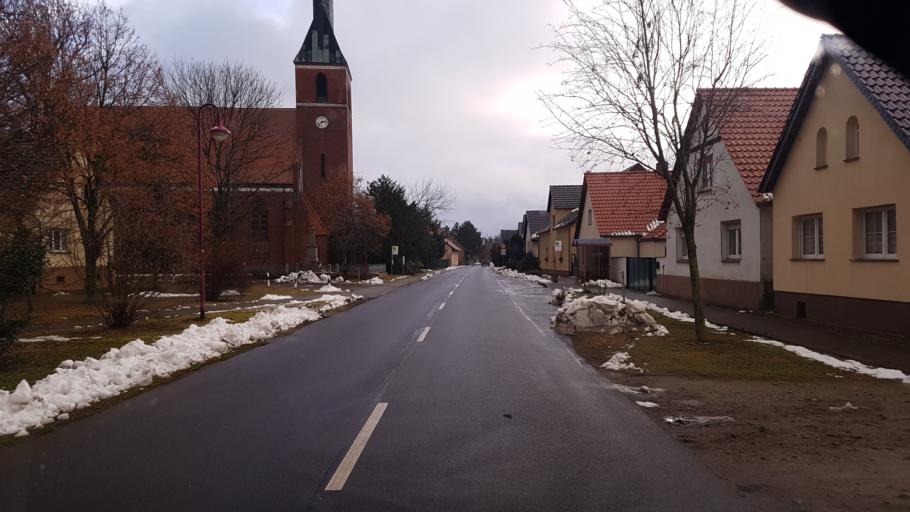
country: DE
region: Brandenburg
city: Heinersbruck
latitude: 51.8179
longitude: 14.5076
